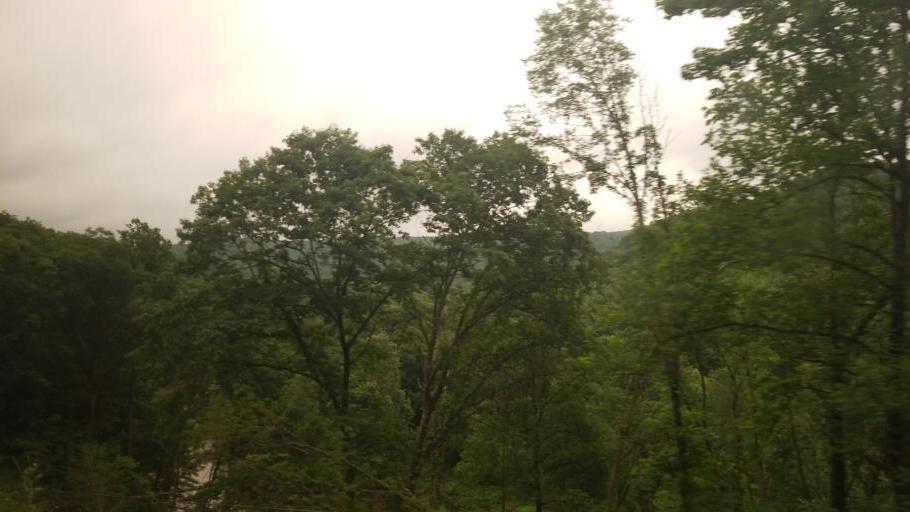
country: US
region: Pennsylvania
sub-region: Somerset County
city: Milford
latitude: 39.8343
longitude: -79.2678
